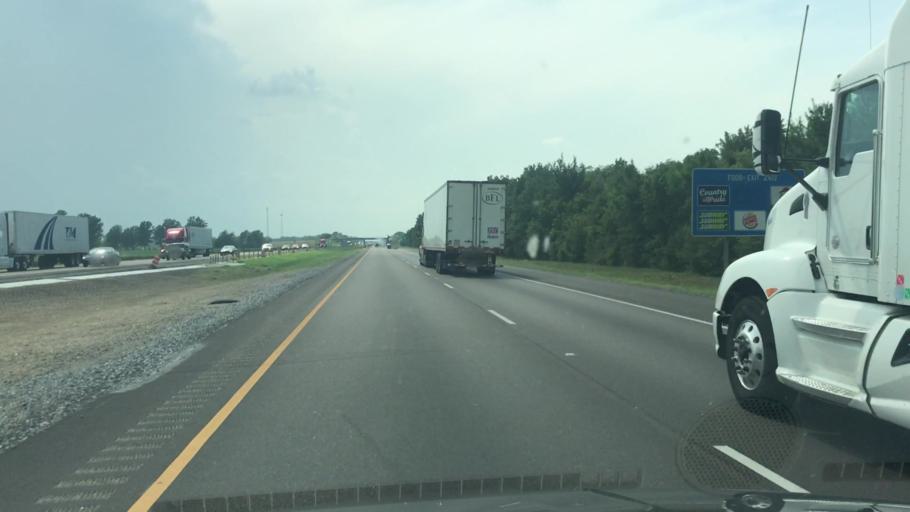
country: US
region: Arkansas
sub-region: Crittenden County
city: Earle
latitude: 35.1337
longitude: -90.4581
